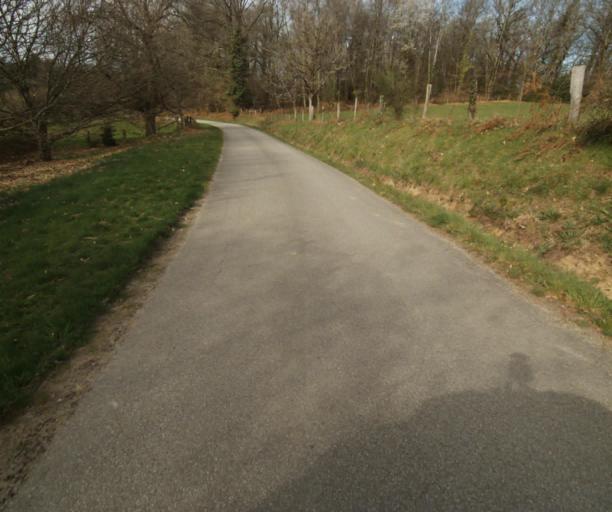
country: FR
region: Limousin
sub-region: Departement de la Correze
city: Correze
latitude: 45.4185
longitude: 1.8142
